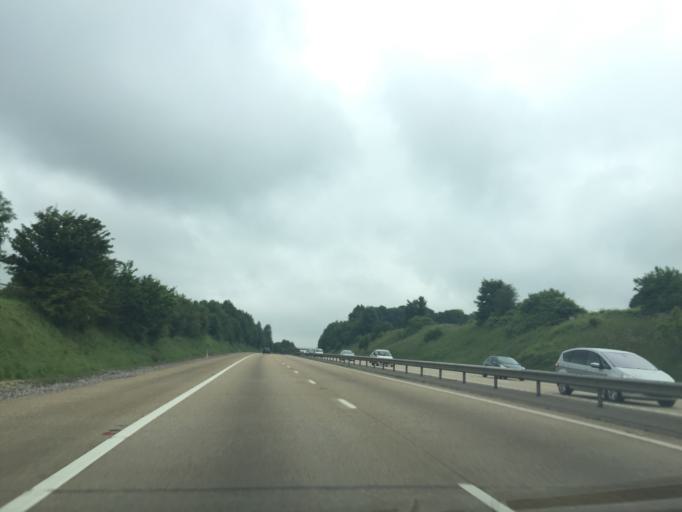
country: GB
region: England
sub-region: Hampshire
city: Overton
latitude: 51.1881
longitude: -1.2095
